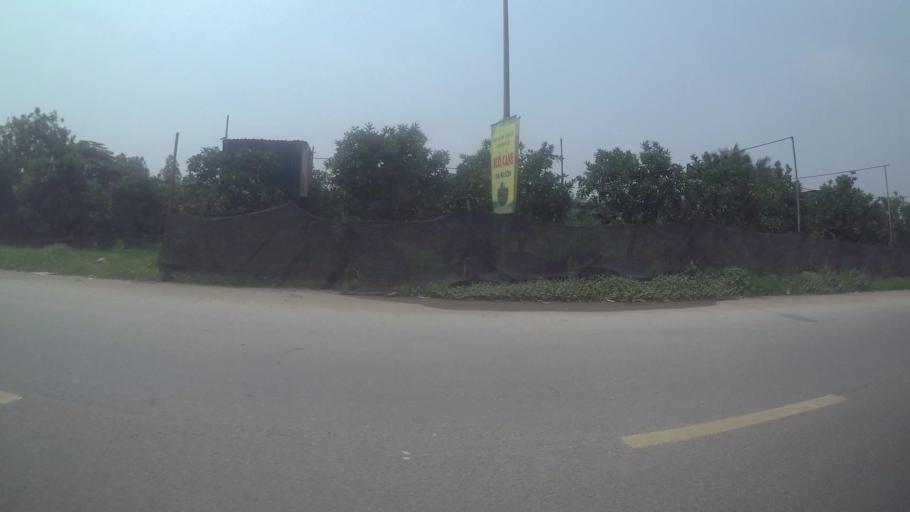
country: VN
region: Ha Noi
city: Quoc Oai
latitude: 21.0036
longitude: 105.6758
